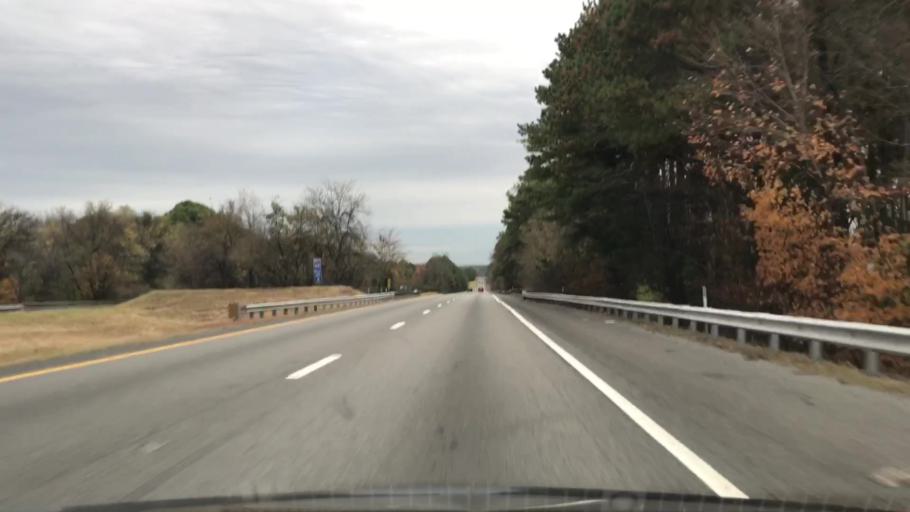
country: US
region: Tennessee
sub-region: Robertson County
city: Cross Plains
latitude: 36.5562
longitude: -86.6278
